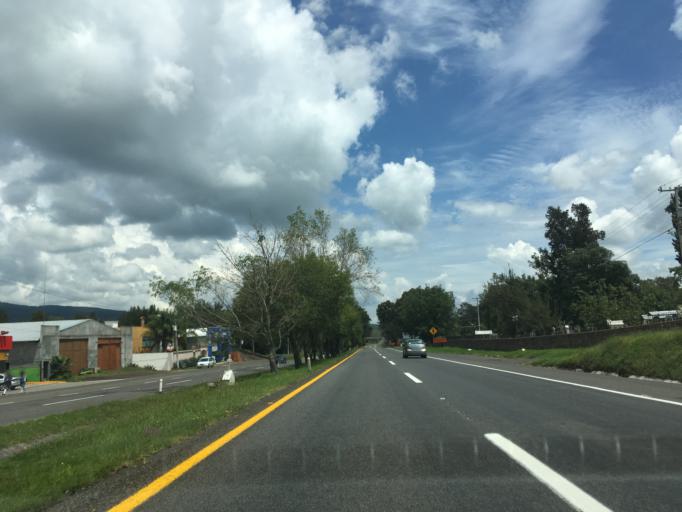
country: MX
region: Michoacan
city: Lagunillas
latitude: 19.5591
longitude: -101.4153
